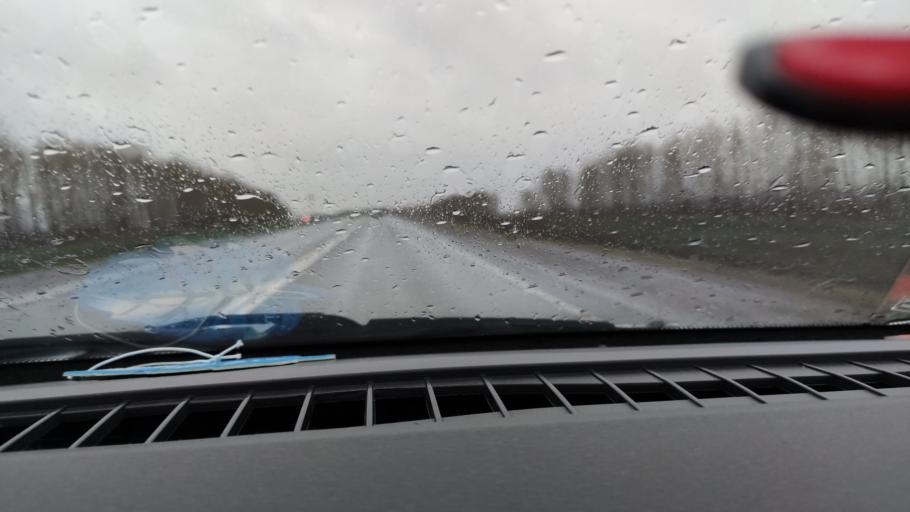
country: RU
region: Tatarstan
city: Mendeleyevsk
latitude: 55.9247
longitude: 52.2768
